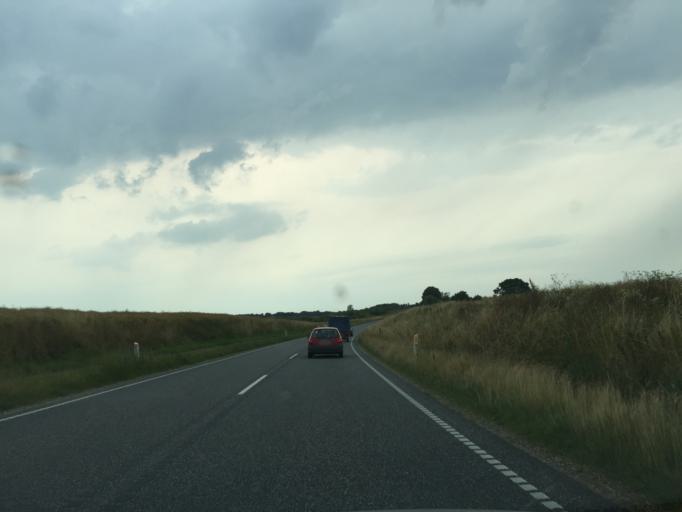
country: DK
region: Central Jutland
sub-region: Silkeborg Kommune
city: Kjellerup
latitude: 56.2986
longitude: 9.4528
